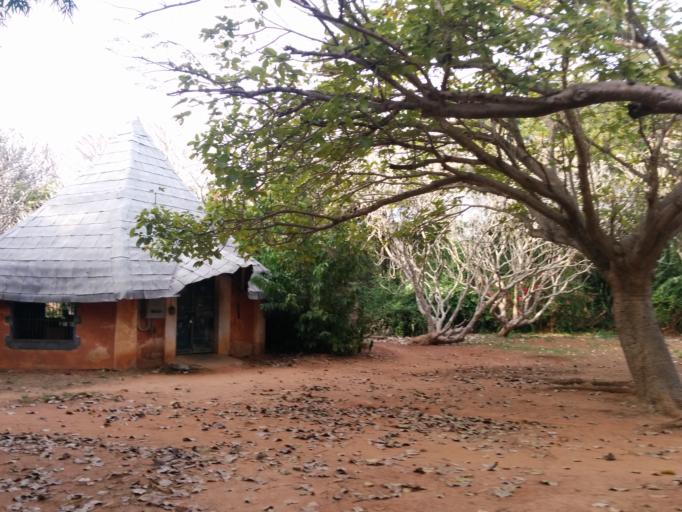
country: IN
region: Tamil Nadu
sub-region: Villupuram
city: Auroville
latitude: 12.0086
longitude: 79.8053
